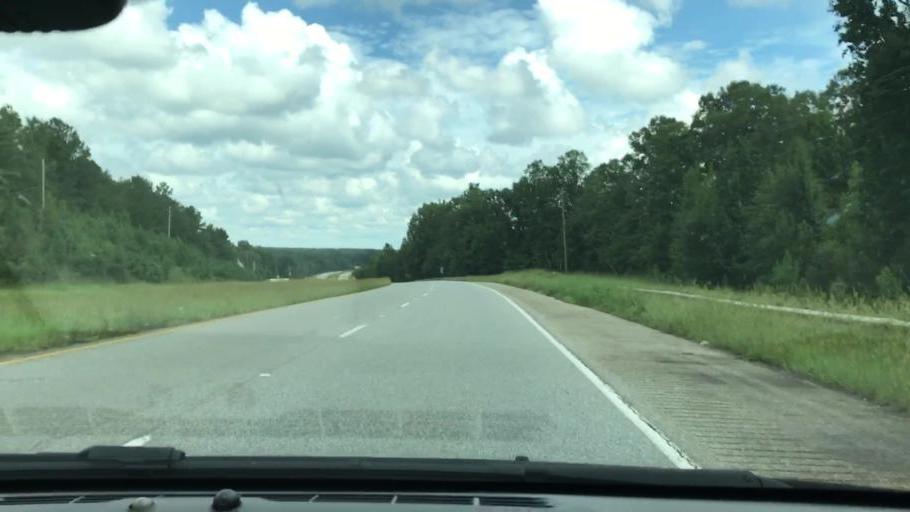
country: US
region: Georgia
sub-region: Stewart County
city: Lumpkin
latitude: 32.1439
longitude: -84.8265
